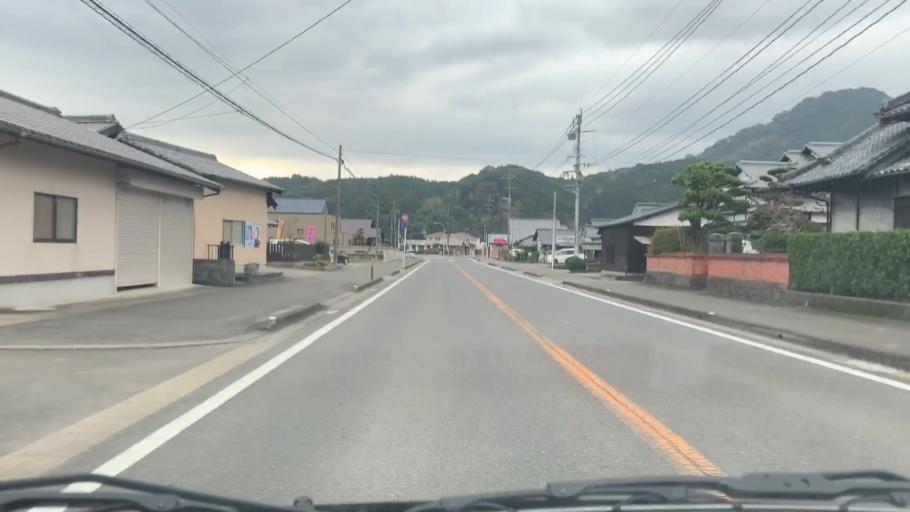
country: JP
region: Saga Prefecture
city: Takeocho-takeo
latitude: 33.1704
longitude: 130.0500
